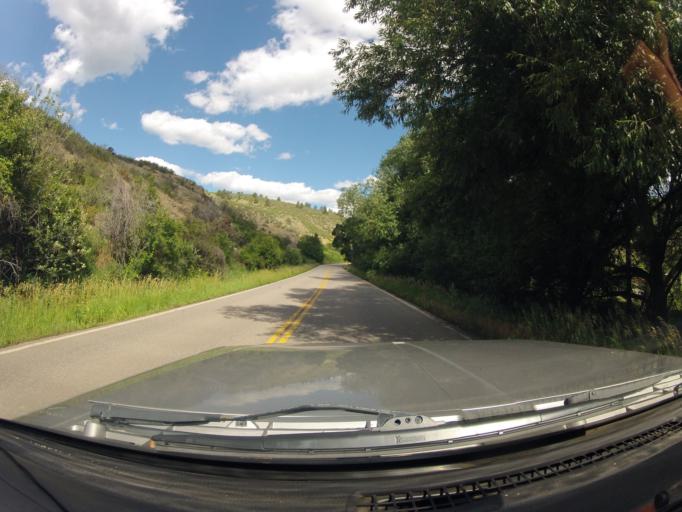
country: US
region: Colorado
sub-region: Larimer County
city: Laporte
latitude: 40.5418
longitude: -105.2812
